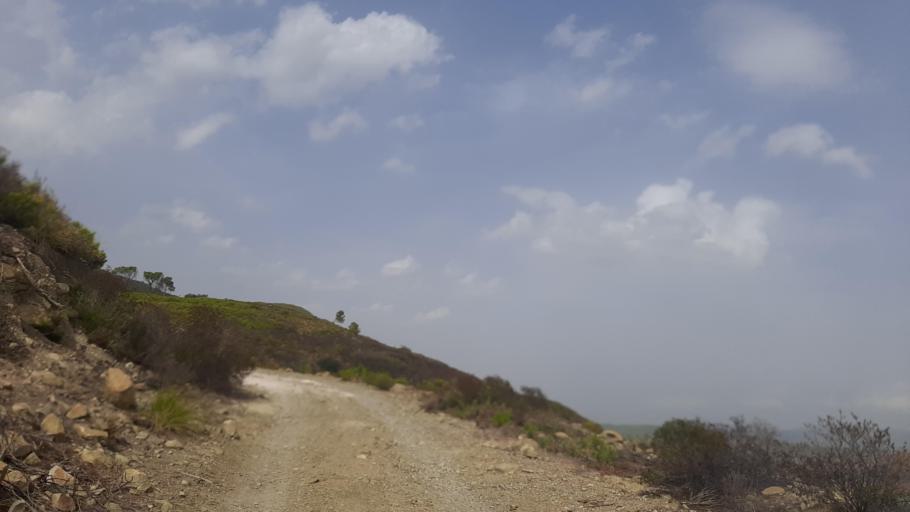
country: TN
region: Zaghwan
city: El Fahs
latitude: 36.1963
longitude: 9.8548
